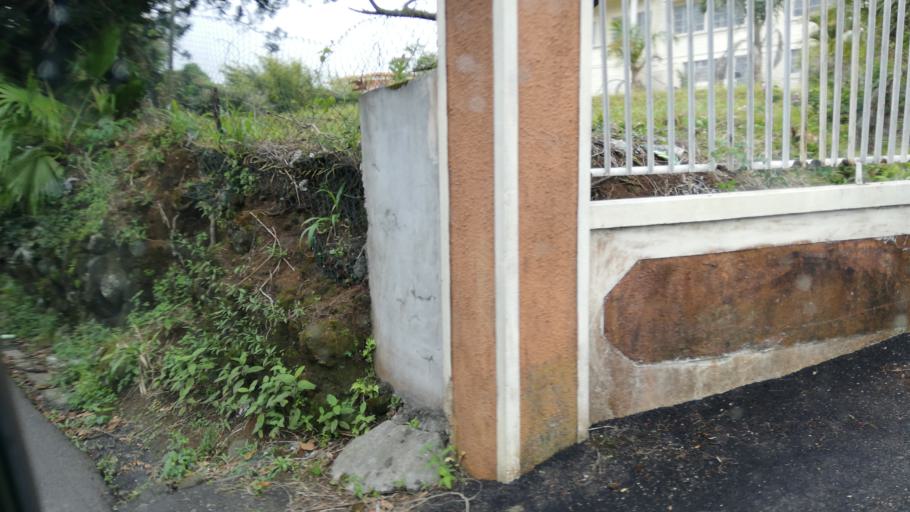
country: MU
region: Plaines Wilhems
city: Curepipe
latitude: -20.3090
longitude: 57.5295
